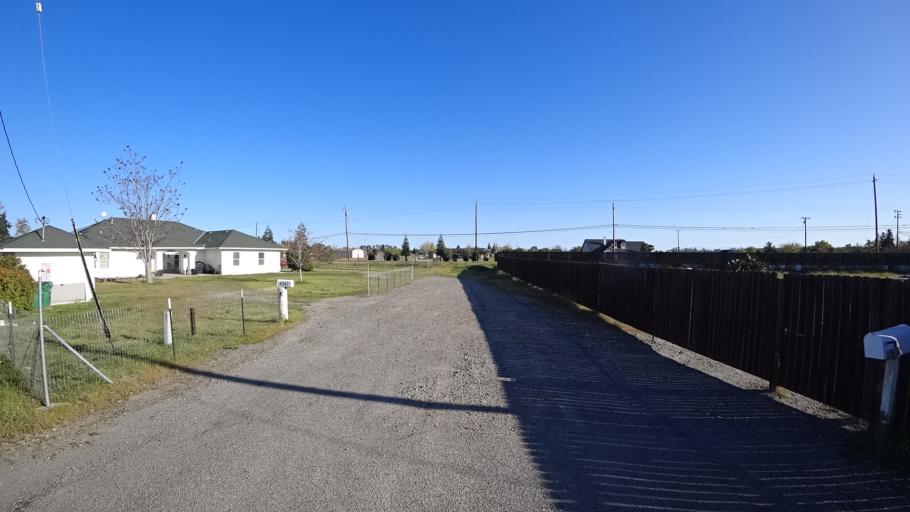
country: US
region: California
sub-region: Glenn County
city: Orland
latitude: 39.7587
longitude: -122.2270
